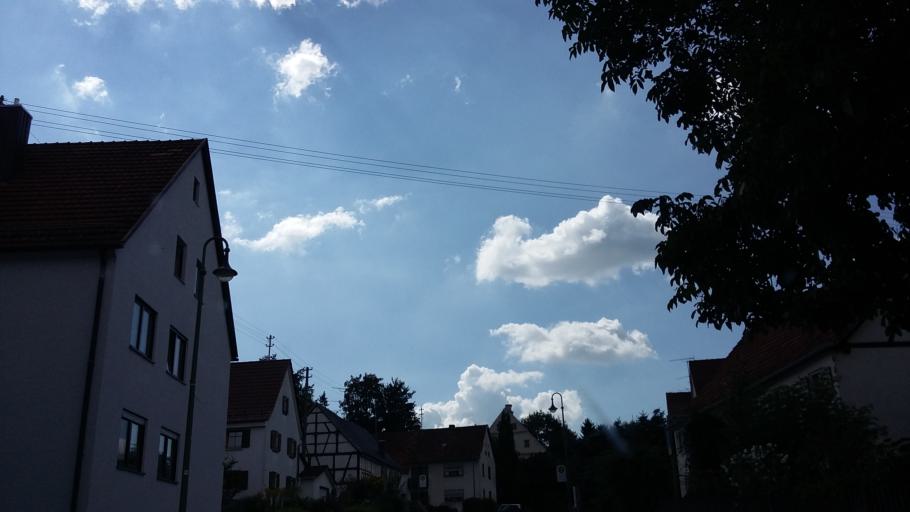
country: DE
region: Bavaria
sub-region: Swabia
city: Pfaffenhofen an der Roth
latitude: 48.3577
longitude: 10.1886
